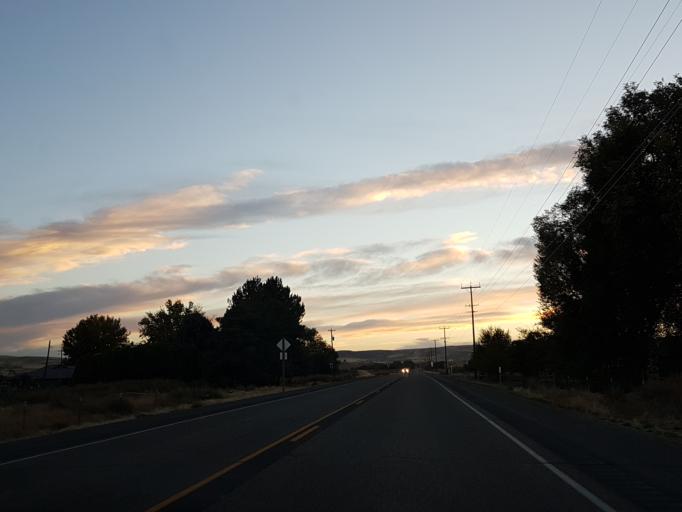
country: US
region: Oregon
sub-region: Malheur County
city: Vale
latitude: 43.9385
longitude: -117.3740
